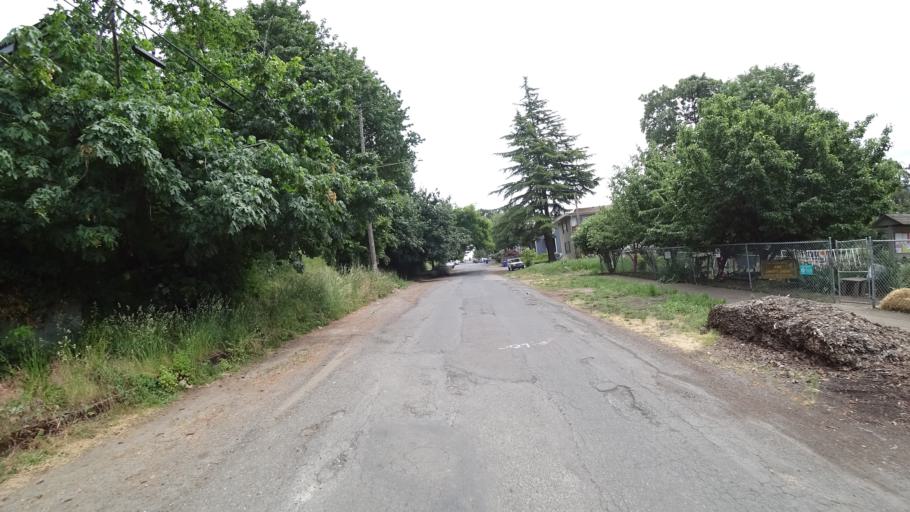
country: US
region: Oregon
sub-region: Washington County
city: West Haven
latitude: 45.5865
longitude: -122.7554
